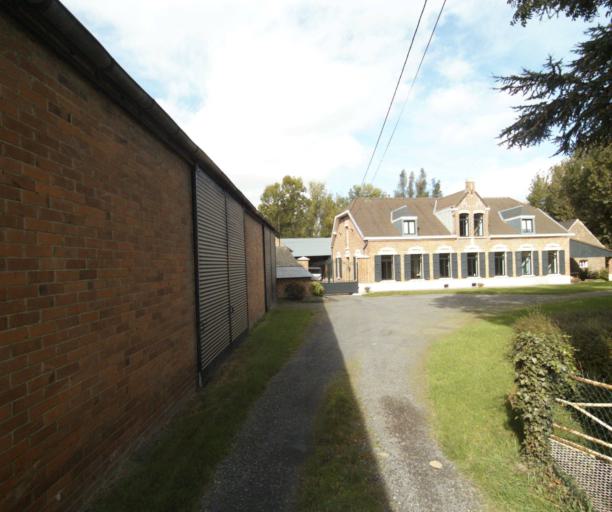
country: FR
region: Nord-Pas-de-Calais
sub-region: Departement du Nord
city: Houplines
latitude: 50.6916
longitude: 2.9062
